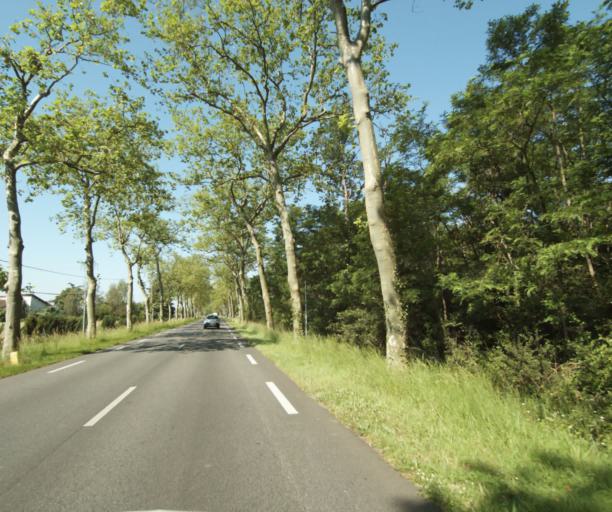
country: FR
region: Midi-Pyrenees
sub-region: Departement du Tarn-et-Garonne
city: Montbeton
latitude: 43.9831
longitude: 1.2968
